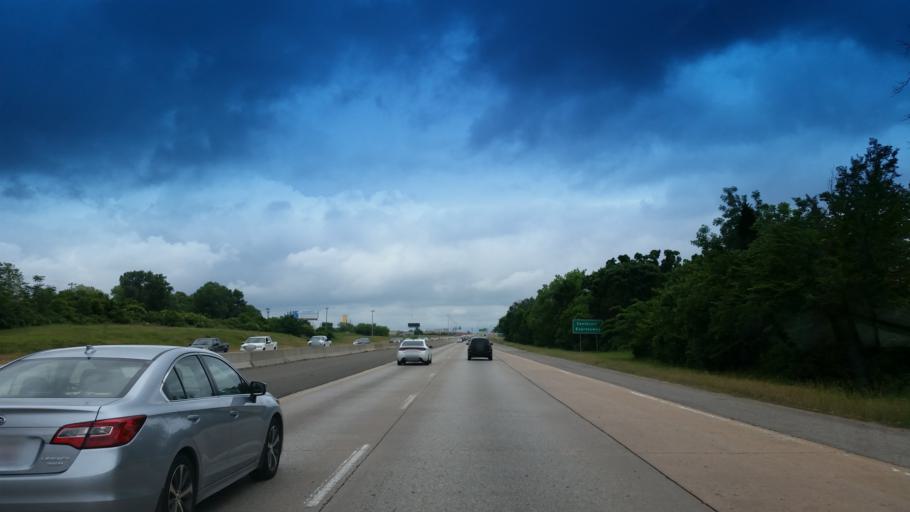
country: US
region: Oklahoma
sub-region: Oklahoma County
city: Nichols Hills
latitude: 35.5179
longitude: -97.5174
